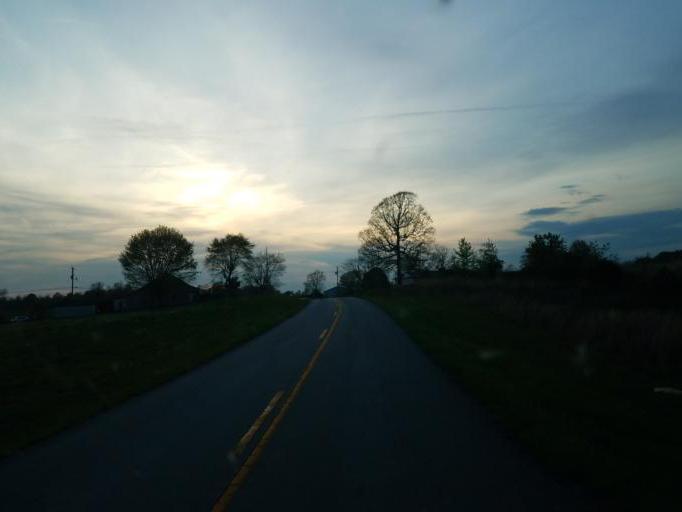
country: US
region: Kentucky
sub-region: Hart County
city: Munfordville
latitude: 37.2388
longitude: -85.7211
